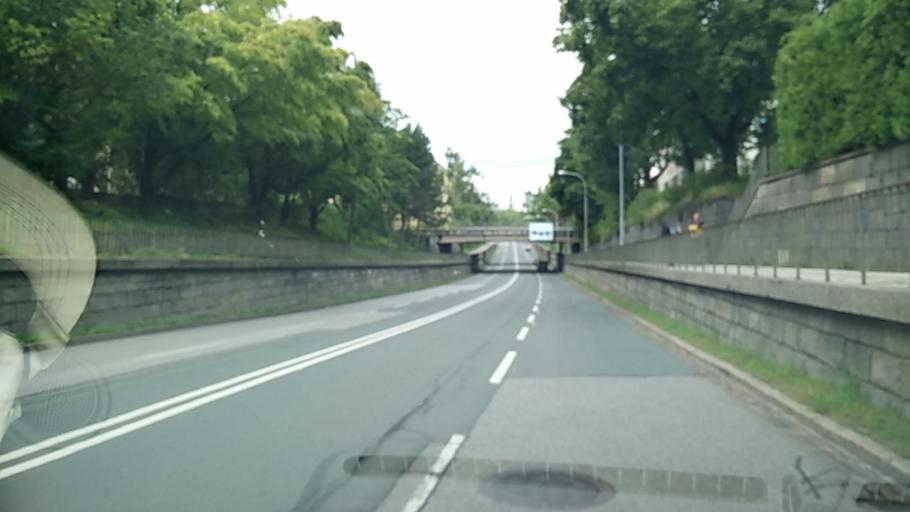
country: AT
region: Carinthia
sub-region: Klagenfurt am Woerthersee
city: Klagenfurt am Woerthersee
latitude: 46.6254
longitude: 14.3230
